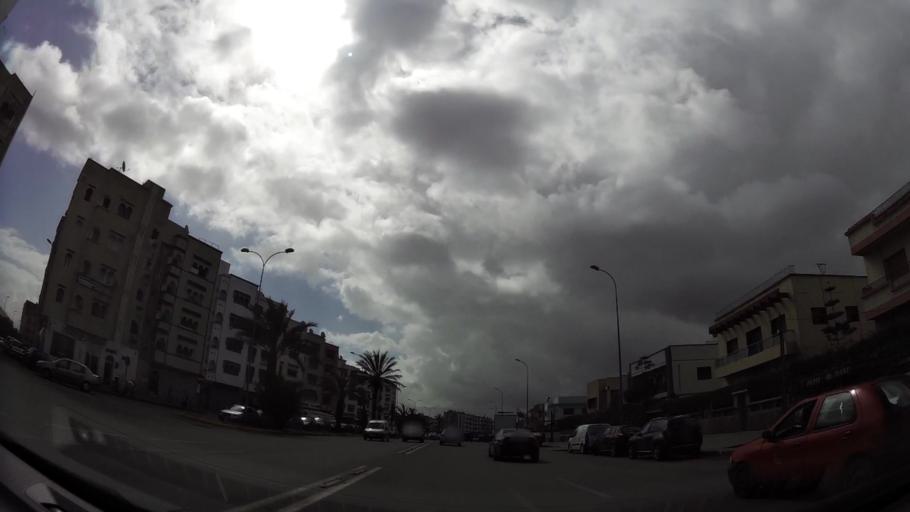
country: MA
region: Grand Casablanca
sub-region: Casablanca
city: Casablanca
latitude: 33.5529
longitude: -7.6039
